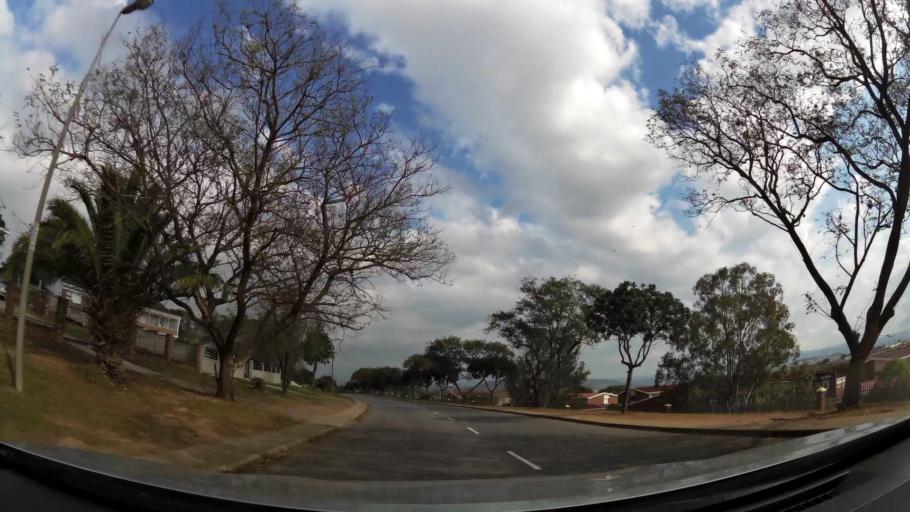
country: ZA
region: Eastern Cape
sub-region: Nelson Mandela Bay Metropolitan Municipality
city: Uitenhage
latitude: -33.7382
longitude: 25.4047
